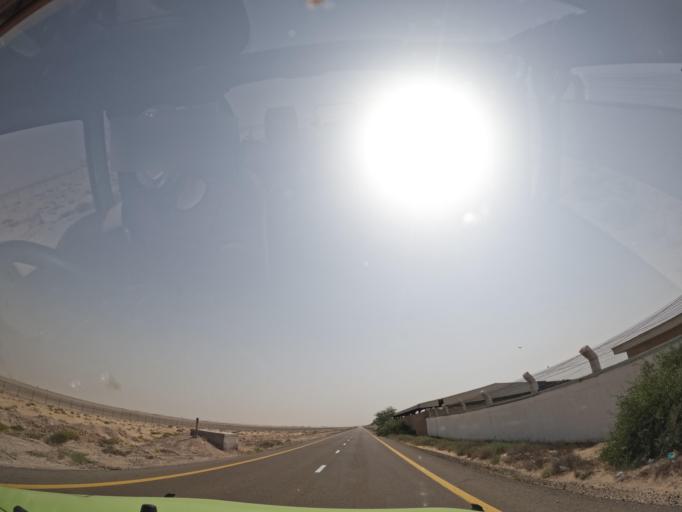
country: AE
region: Dubai
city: Dubai
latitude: 24.6267
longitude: 55.4029
